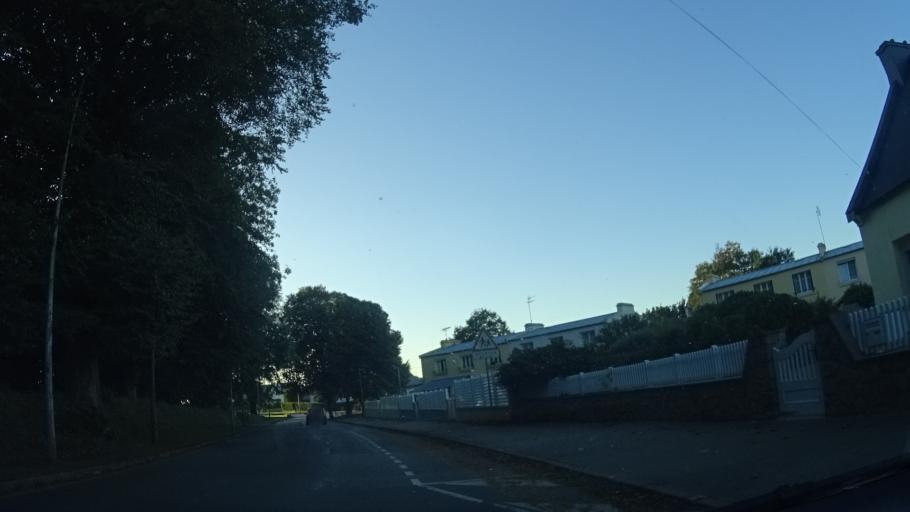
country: FR
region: Brittany
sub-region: Departement du Finistere
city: Guilers
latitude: 48.4244
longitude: -4.5640
